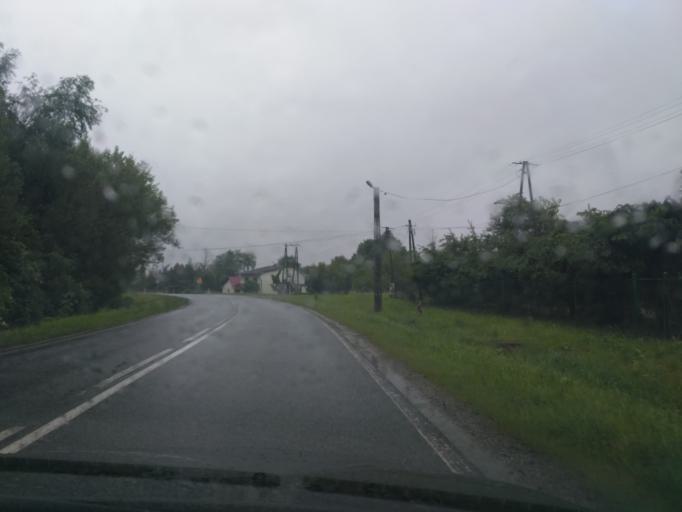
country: PL
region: Subcarpathian Voivodeship
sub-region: Powiat krosnienski
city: Leki
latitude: 49.8017
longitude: 21.6419
